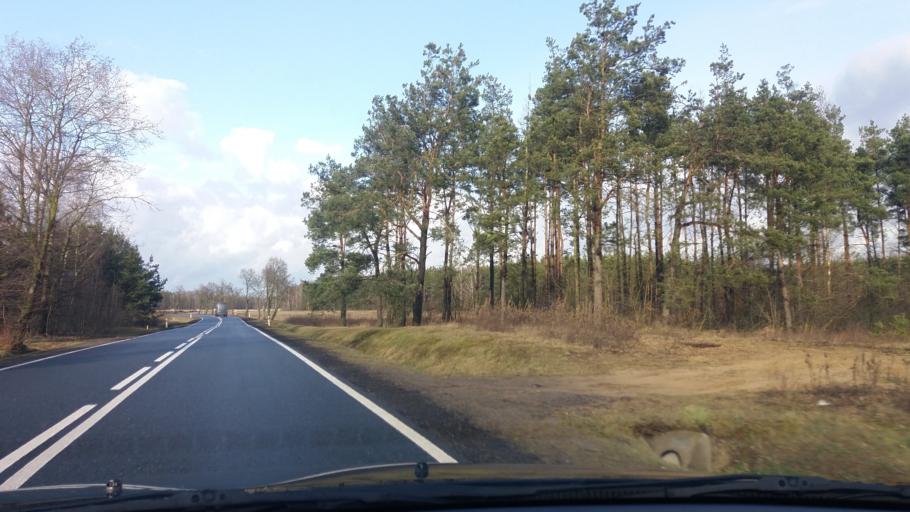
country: PL
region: Masovian Voivodeship
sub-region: Powiat przasnyski
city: Chorzele
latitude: 53.2718
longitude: 20.8996
